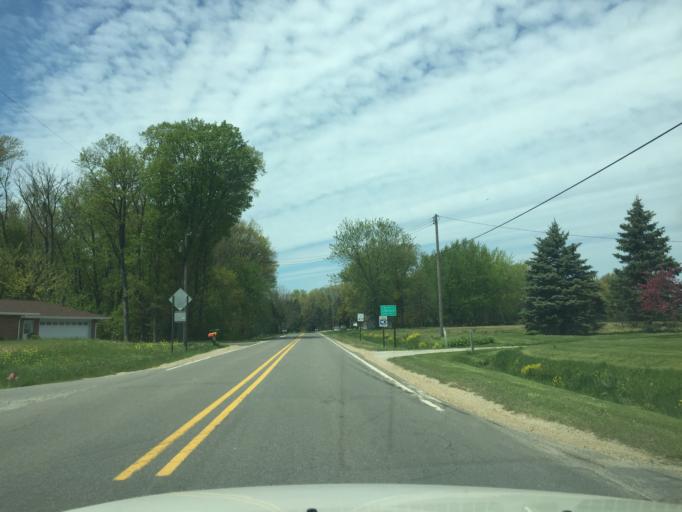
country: US
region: Michigan
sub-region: Berrien County
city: Stevensville
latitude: 41.9854
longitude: -86.4991
